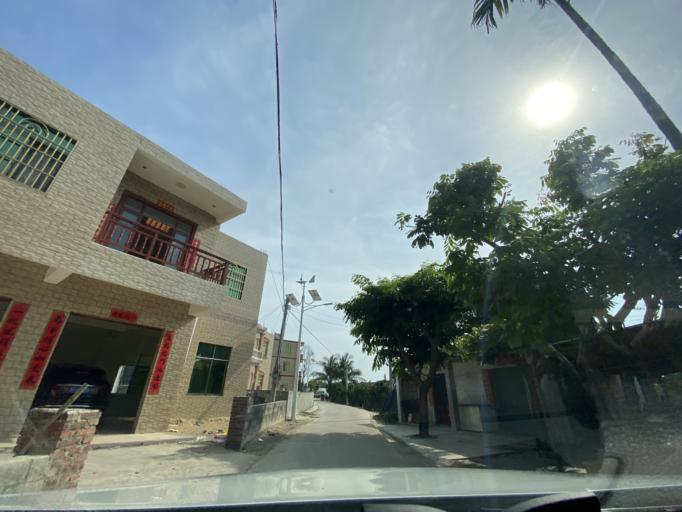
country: CN
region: Hainan
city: Yingzhou
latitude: 18.4076
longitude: 109.8313
